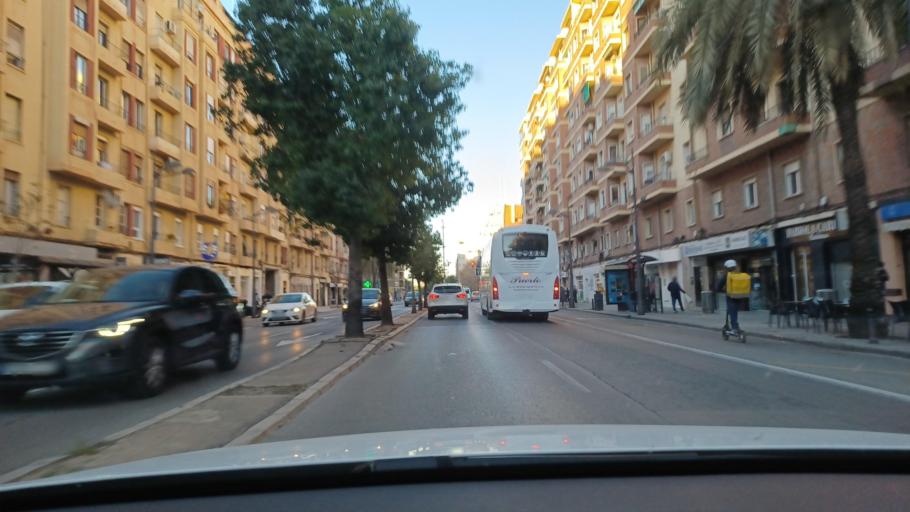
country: ES
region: Valencia
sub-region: Provincia de Valencia
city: Valencia
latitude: 39.4739
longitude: -0.3532
